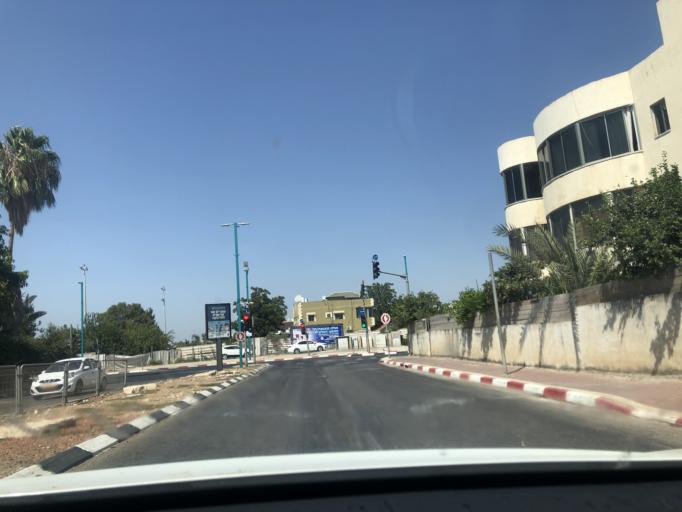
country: IL
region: Central District
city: Lod
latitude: 31.9588
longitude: 34.8916
